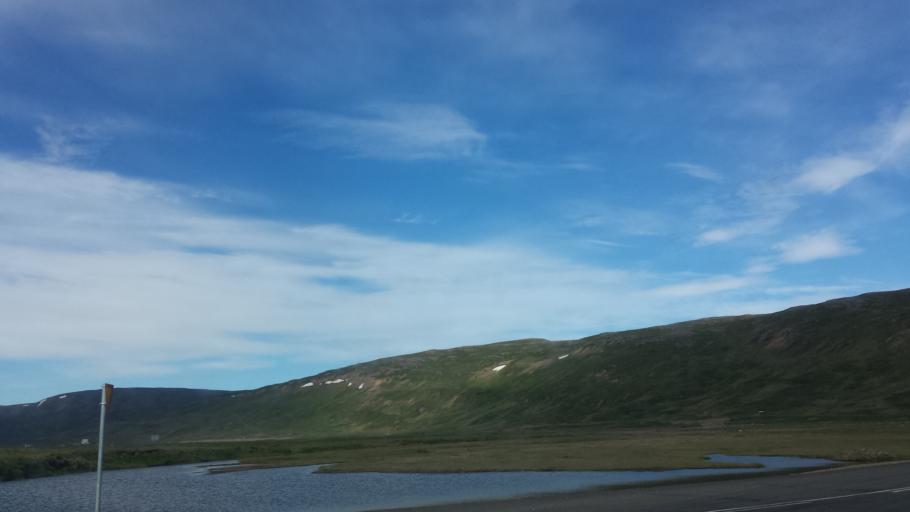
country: IS
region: West
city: Stykkisholmur
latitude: 65.7642
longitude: -21.7805
